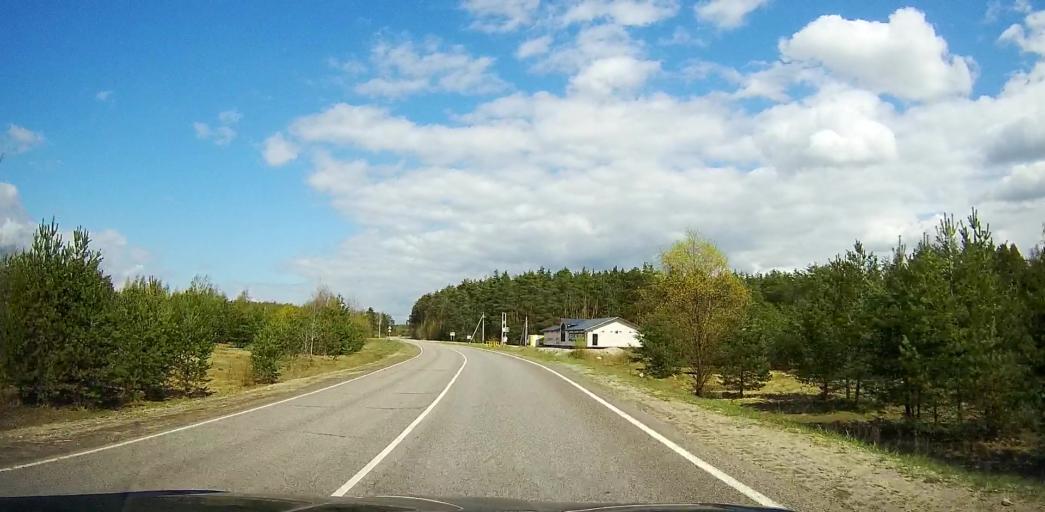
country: RU
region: Moskovskaya
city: Davydovo
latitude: 55.5485
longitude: 38.8165
